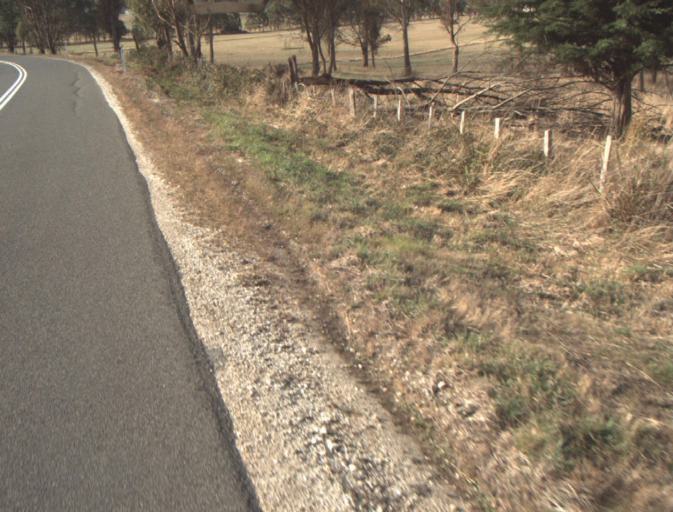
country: AU
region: Tasmania
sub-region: Launceston
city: Mayfield
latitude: -41.2263
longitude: 147.1227
